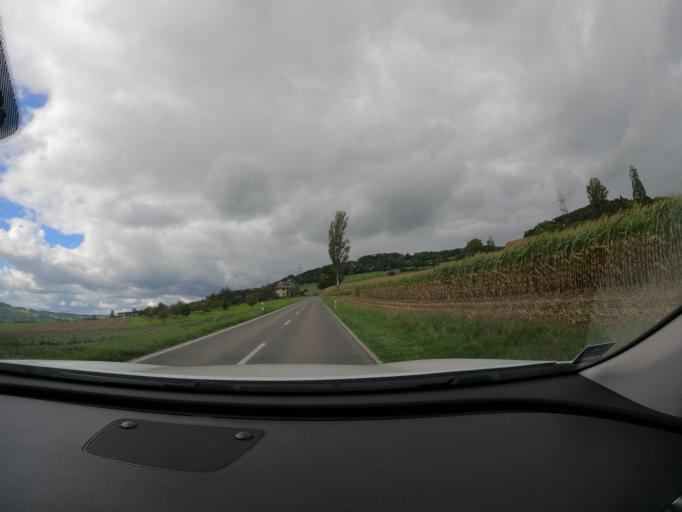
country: CH
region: Lucerne
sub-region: Sursee District
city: Bueron
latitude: 47.2183
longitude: 8.0991
